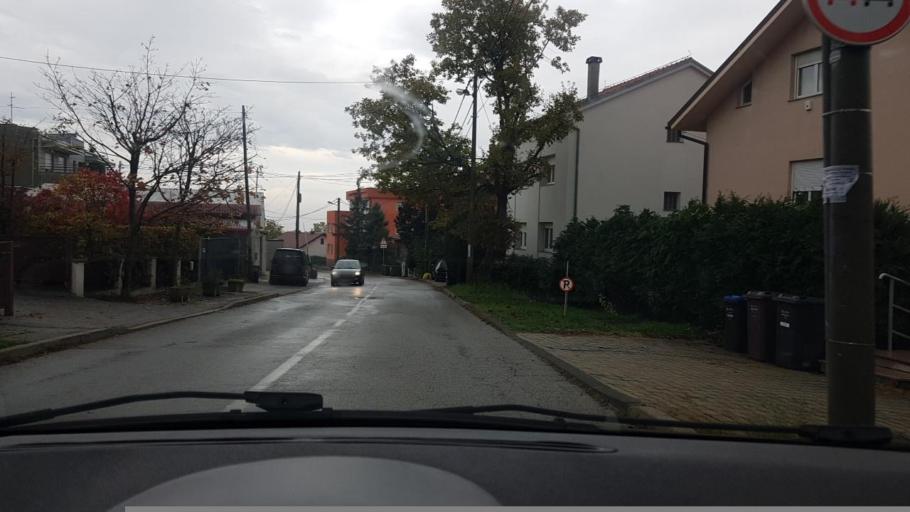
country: HR
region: Grad Zagreb
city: Zagreb
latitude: 45.8505
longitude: 15.9850
